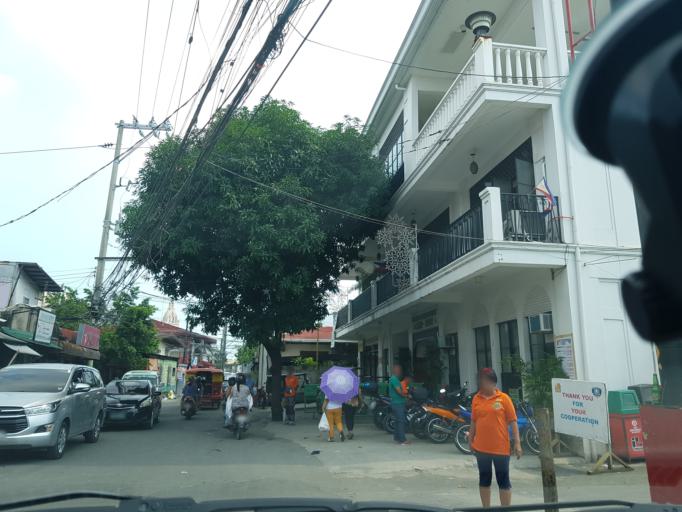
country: PH
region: Calabarzon
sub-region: Province of Rizal
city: Pateros
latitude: 14.5423
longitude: 121.0802
